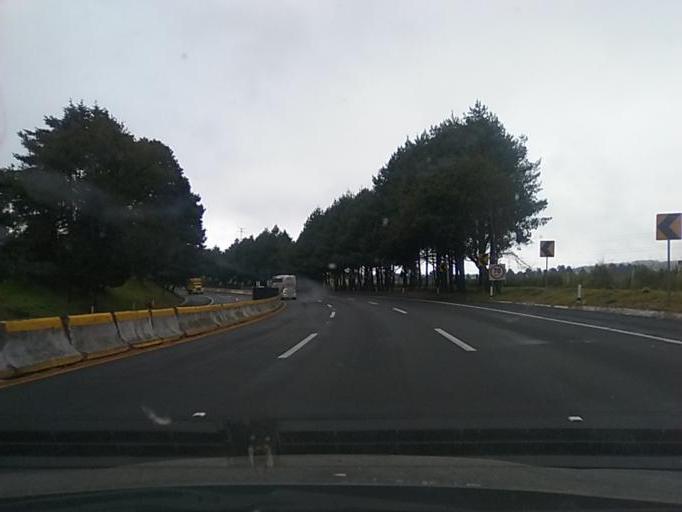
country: MX
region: Mexico City
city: Xochimilco
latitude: 19.1656
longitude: -99.1524
